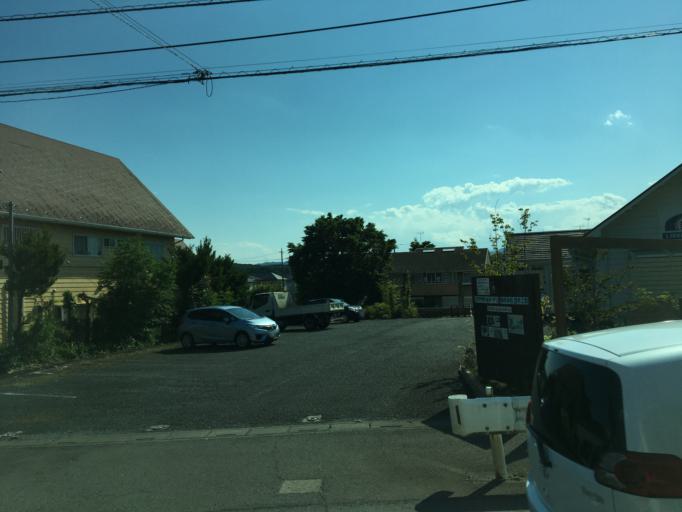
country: JP
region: Saitama
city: Morohongo
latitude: 35.9710
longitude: 139.3402
